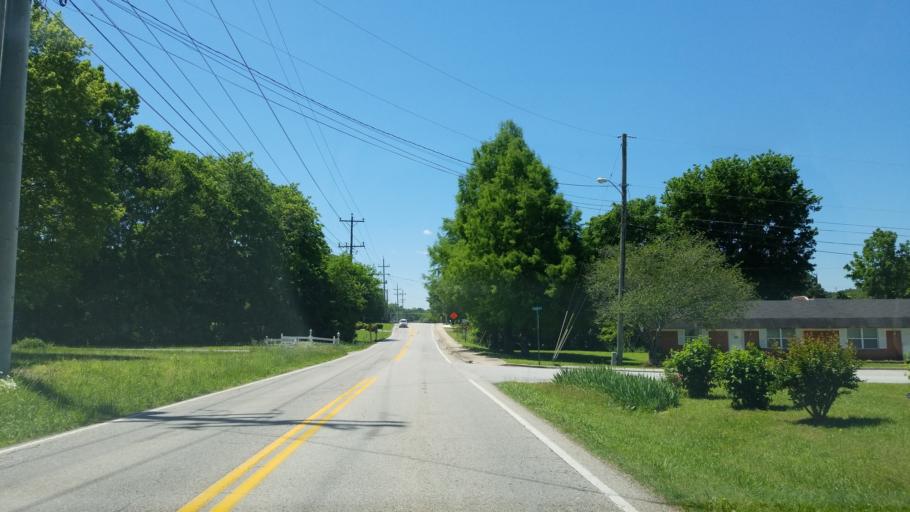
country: US
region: Tennessee
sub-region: Hamilton County
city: Collegedale
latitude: 35.0658
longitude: -85.0649
